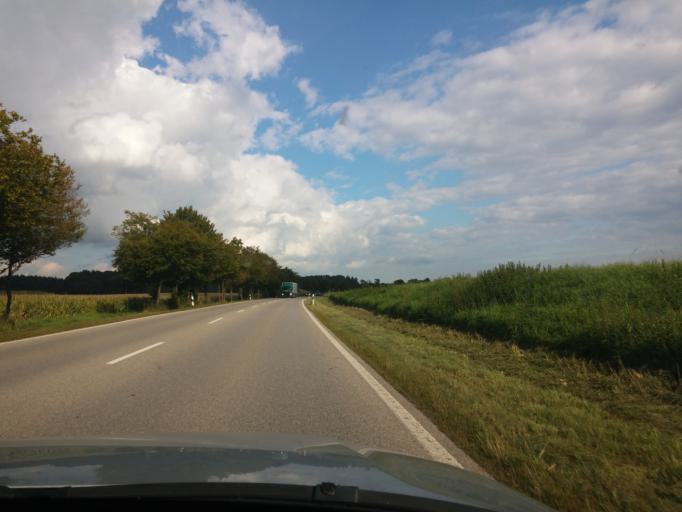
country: DE
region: Bavaria
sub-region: Upper Bavaria
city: Kirchseeon
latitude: 48.0703
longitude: 11.9135
